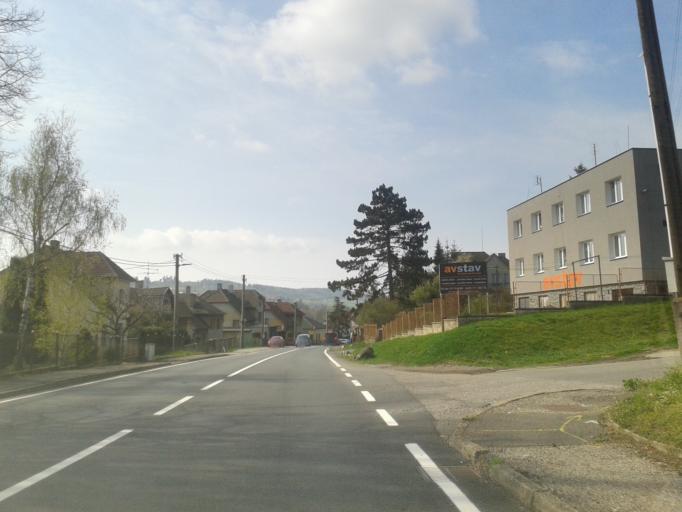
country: CZ
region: Central Bohemia
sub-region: Okres Beroun
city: Horovice
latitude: 49.8463
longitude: 13.9066
